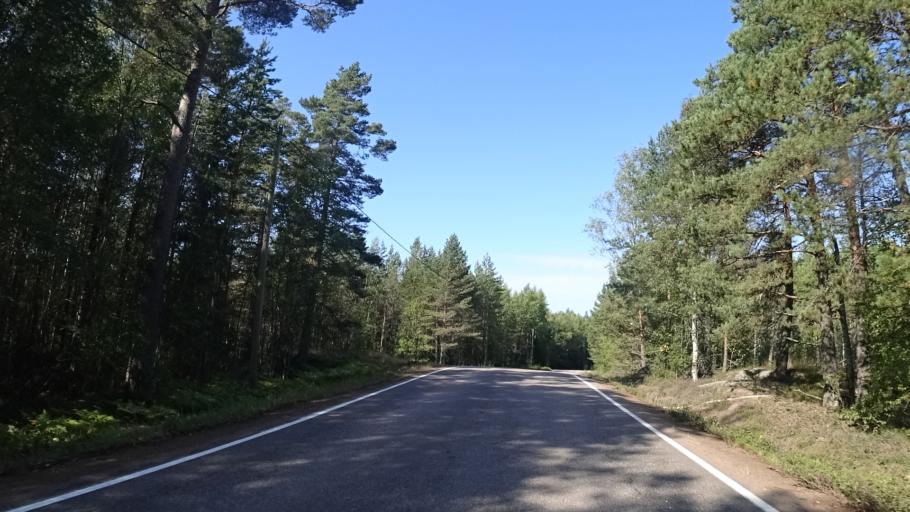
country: FI
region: Kymenlaakso
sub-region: Kotka-Hamina
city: Hamina
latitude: 60.5534
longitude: 27.2456
